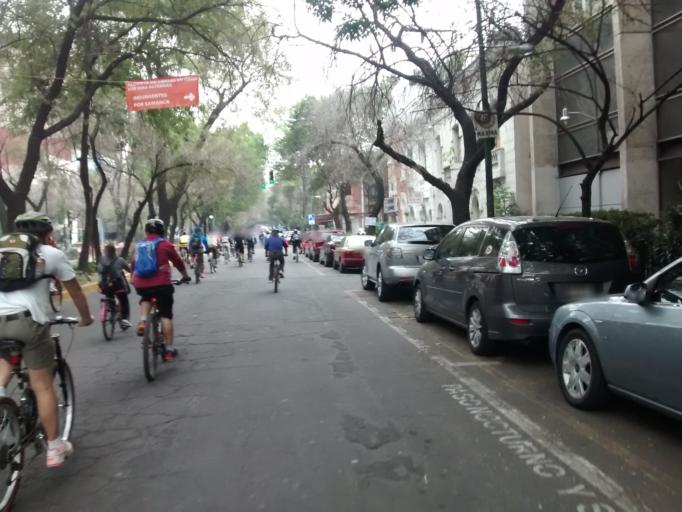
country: MX
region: Mexico City
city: Benito Juarez
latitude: 19.4188
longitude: -99.1715
